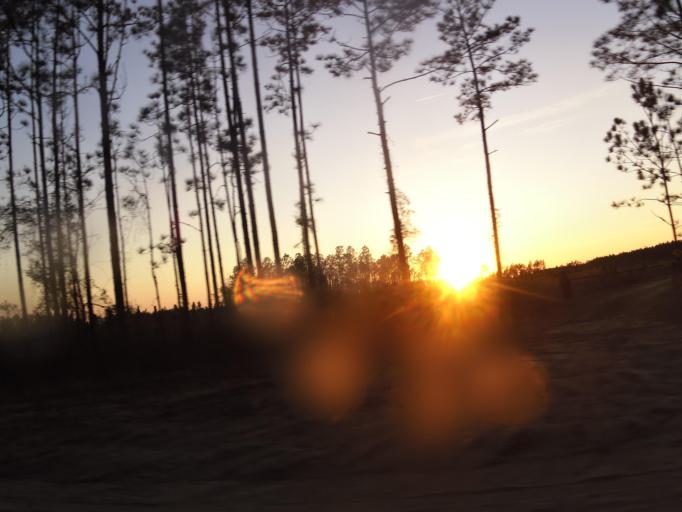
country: US
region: Florida
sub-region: Clay County
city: Asbury Lake
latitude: 29.9377
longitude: -81.7853
